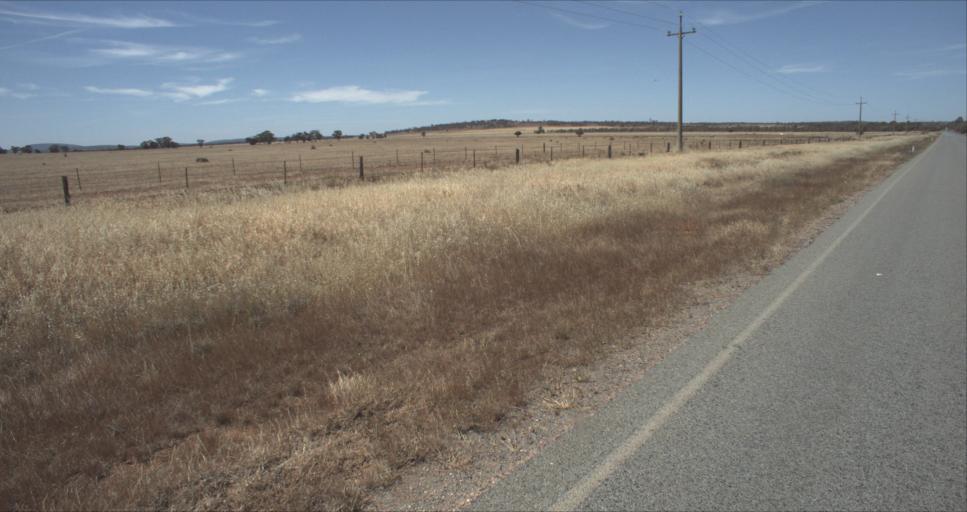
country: AU
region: New South Wales
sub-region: Leeton
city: Leeton
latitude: -34.6275
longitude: 146.4530
